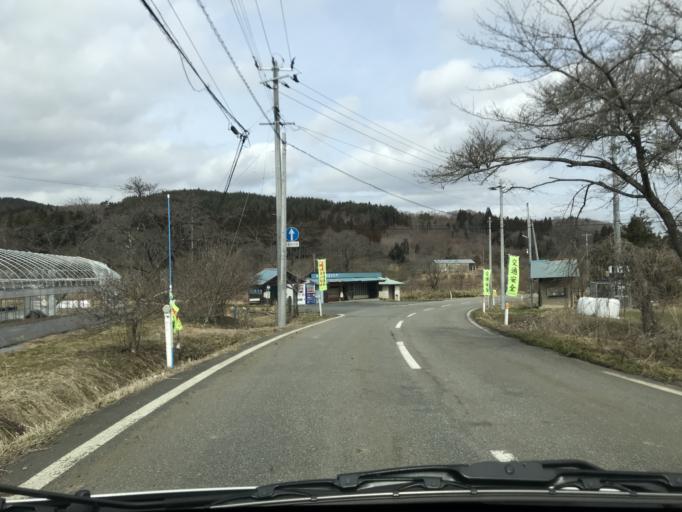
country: JP
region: Iwate
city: Kitakami
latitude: 39.2608
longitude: 141.3163
